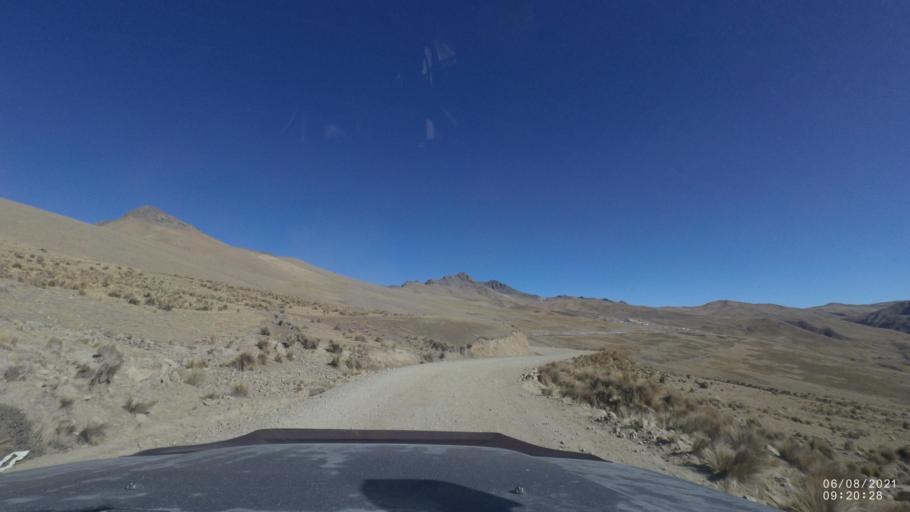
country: BO
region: Cochabamba
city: Colchani
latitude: -17.0247
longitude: -66.5394
